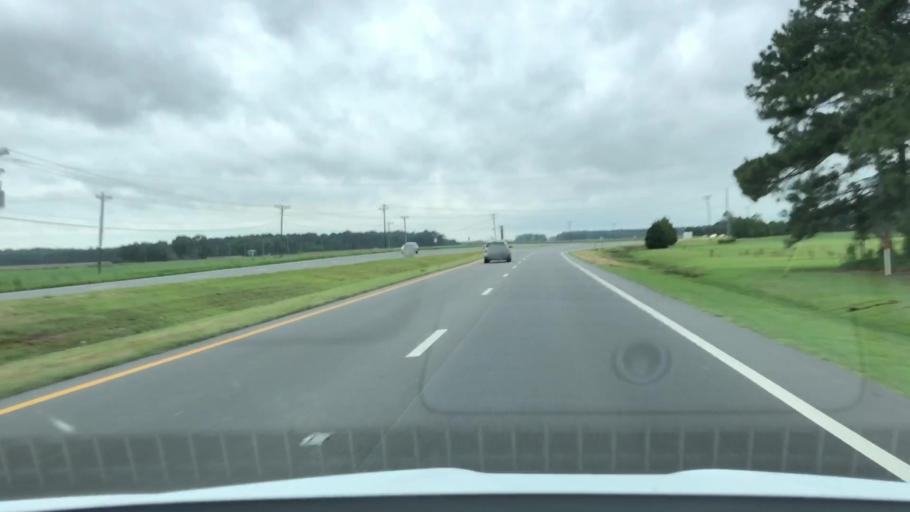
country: US
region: North Carolina
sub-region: Lenoir County
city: La Grange
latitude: 35.2603
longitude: -77.7109
